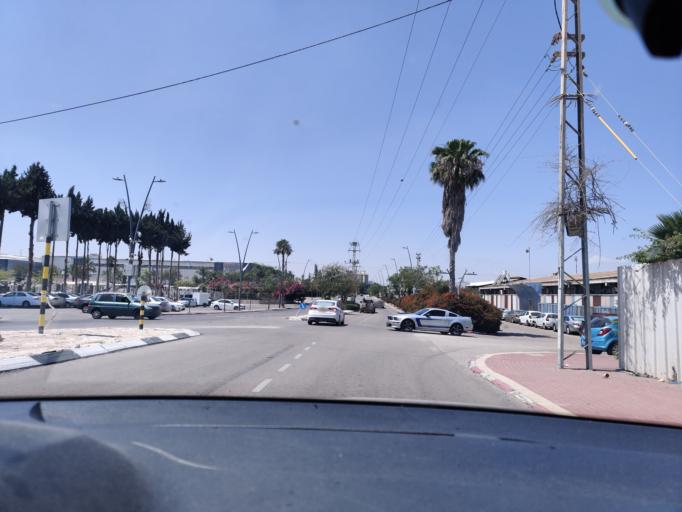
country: IL
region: Southern District
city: Qiryat Gat
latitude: 31.6075
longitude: 34.7861
